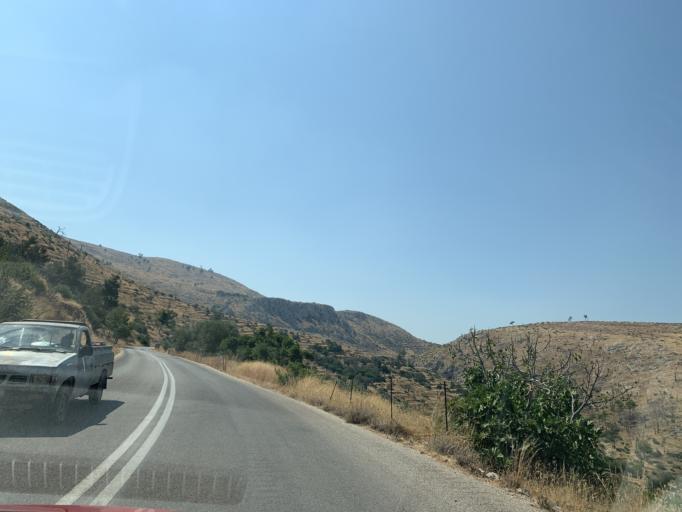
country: GR
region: North Aegean
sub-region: Chios
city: Thymiana
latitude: 38.3238
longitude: 26.0039
